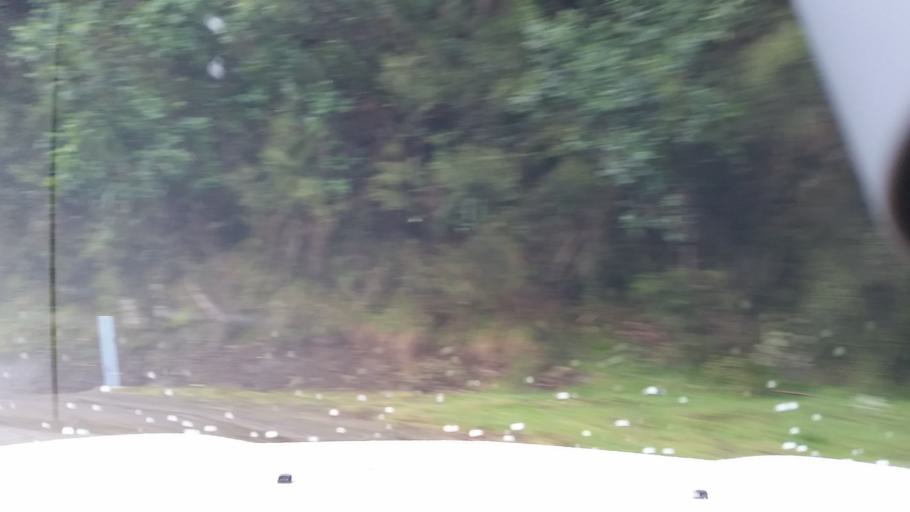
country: NZ
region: Wellington
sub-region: South Wairarapa District
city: Waipawa
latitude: -41.3494
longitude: 175.6781
